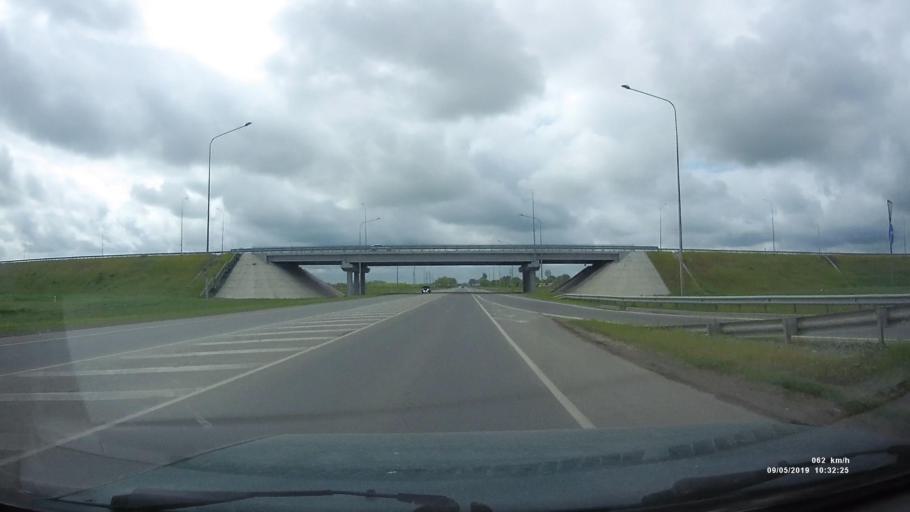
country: RU
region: Rostov
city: Azov
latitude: 47.0726
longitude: 39.4263
